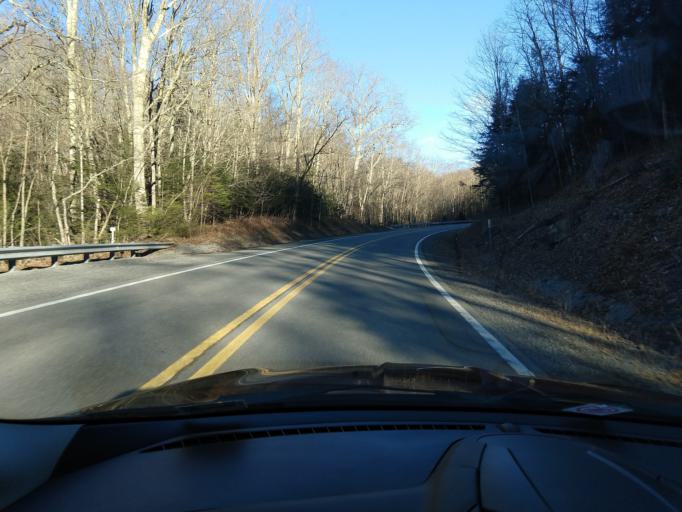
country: US
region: Virginia
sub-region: Highland County
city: Monterey
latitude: 38.5620
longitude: -79.8394
